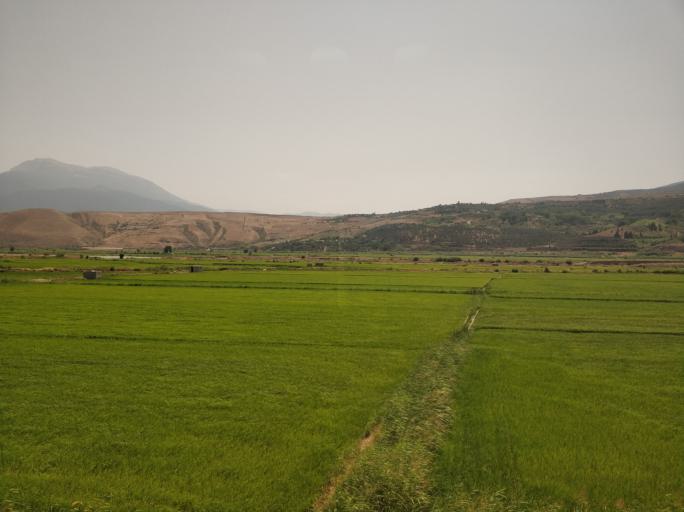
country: IR
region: Gilan
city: Pa'in-e Bazar-e Rudbar
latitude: 36.8788
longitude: 49.4963
